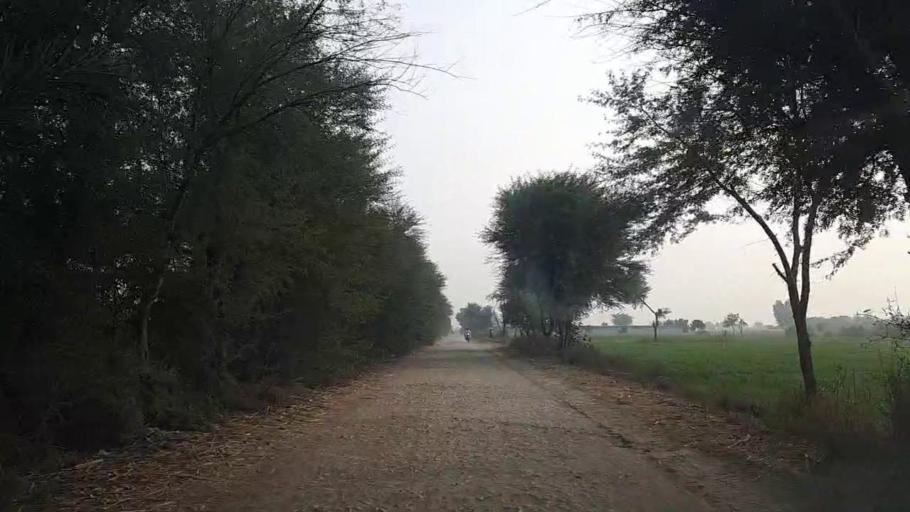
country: PK
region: Sindh
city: Khadro
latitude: 26.1223
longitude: 68.7960
